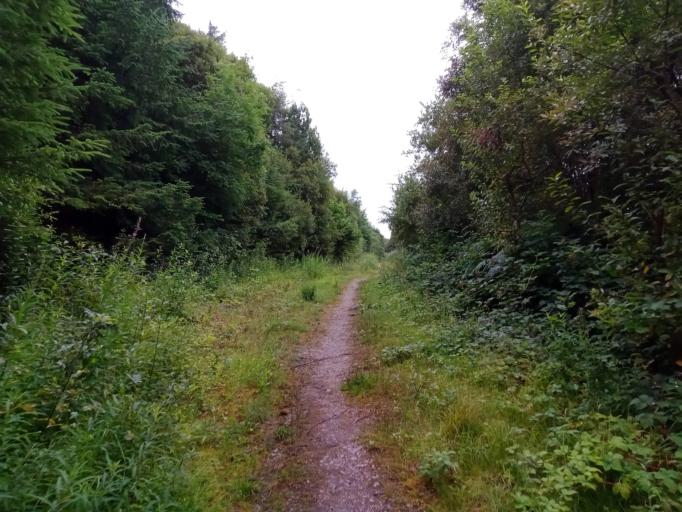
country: IE
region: Leinster
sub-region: Kilkenny
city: Ballyragget
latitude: 52.8200
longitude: -7.4144
